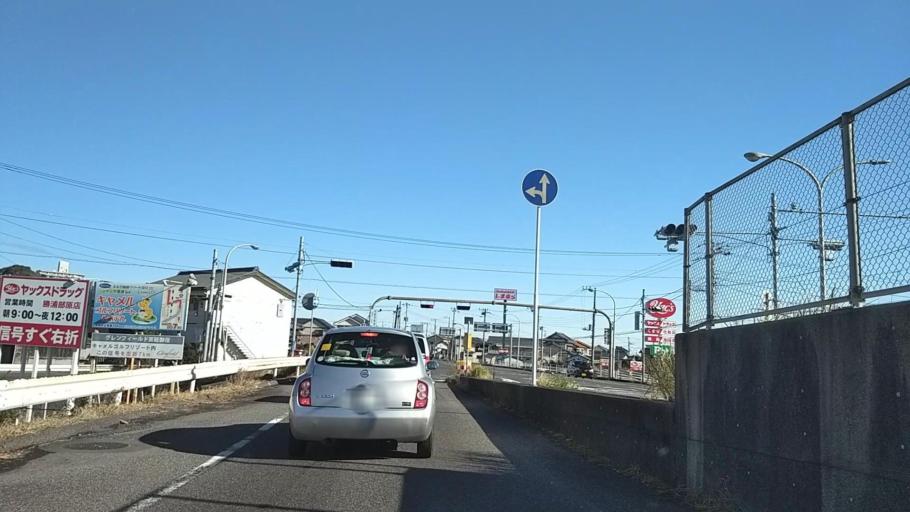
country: JP
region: Chiba
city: Katsuura
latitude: 35.1657
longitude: 140.3299
